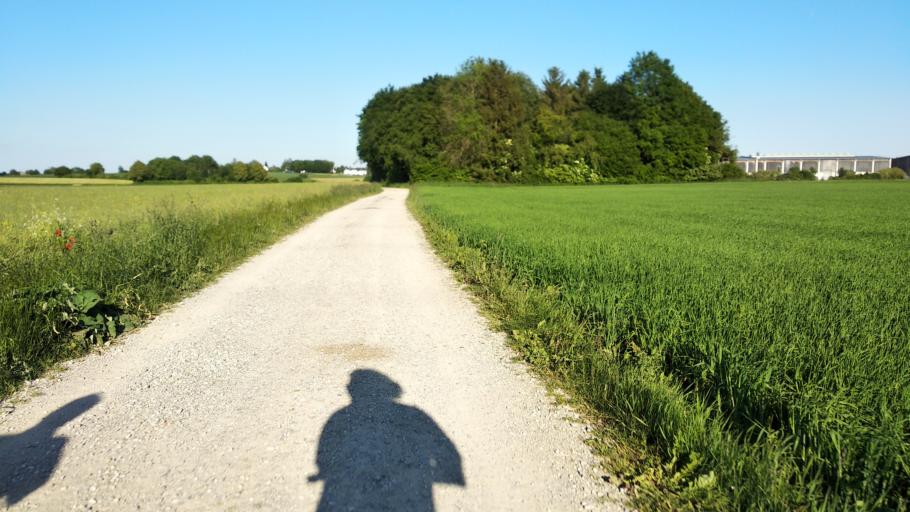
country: DE
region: Bavaria
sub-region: Upper Bavaria
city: Zorneding
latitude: 48.0962
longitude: 11.8162
